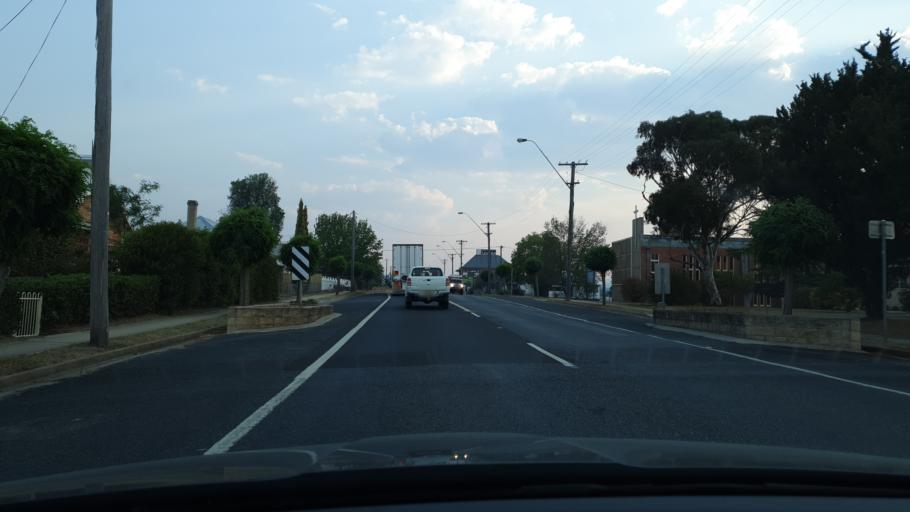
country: AU
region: New South Wales
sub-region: Tenterfield Municipality
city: Carrolls Creek
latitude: -29.0485
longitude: 152.0201
